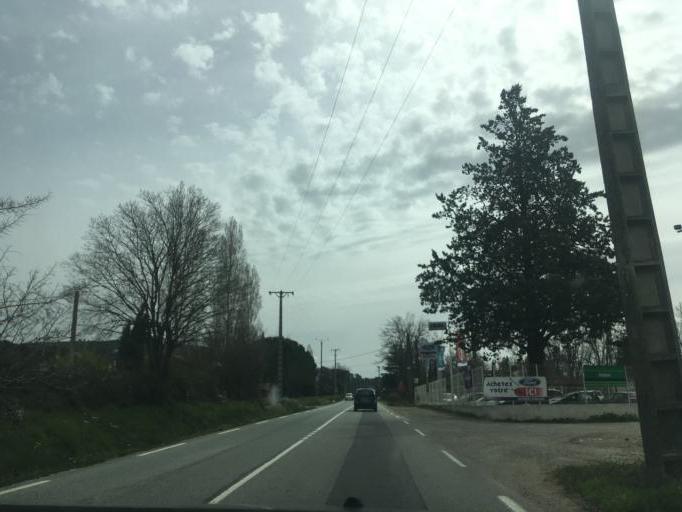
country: FR
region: Provence-Alpes-Cote d'Azur
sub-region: Departement du Var
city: Montauroux
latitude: 43.6041
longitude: 6.7725
